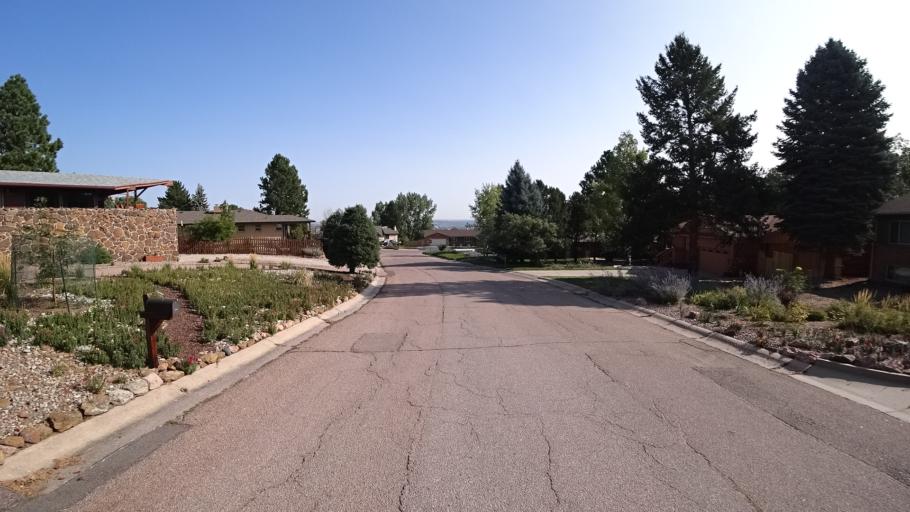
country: US
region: Colorado
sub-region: El Paso County
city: Colorado Springs
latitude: 38.8151
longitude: -104.8637
